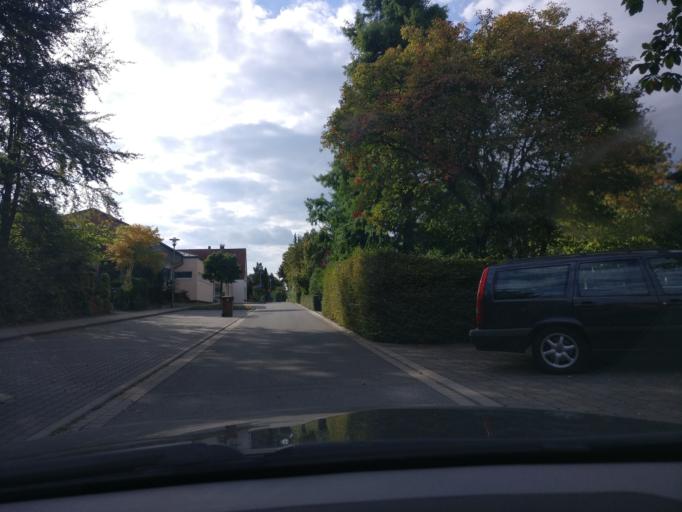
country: DE
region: Lower Saxony
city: Melle
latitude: 52.1865
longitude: 8.3484
